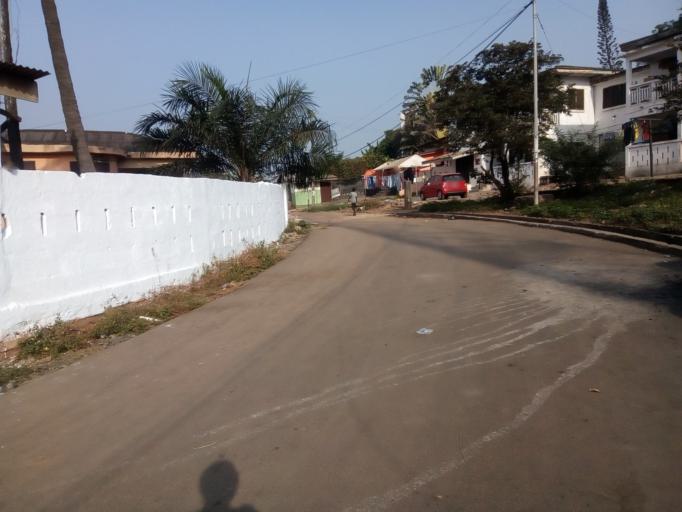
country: GH
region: Greater Accra
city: Accra
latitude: 5.5866
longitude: -0.2148
